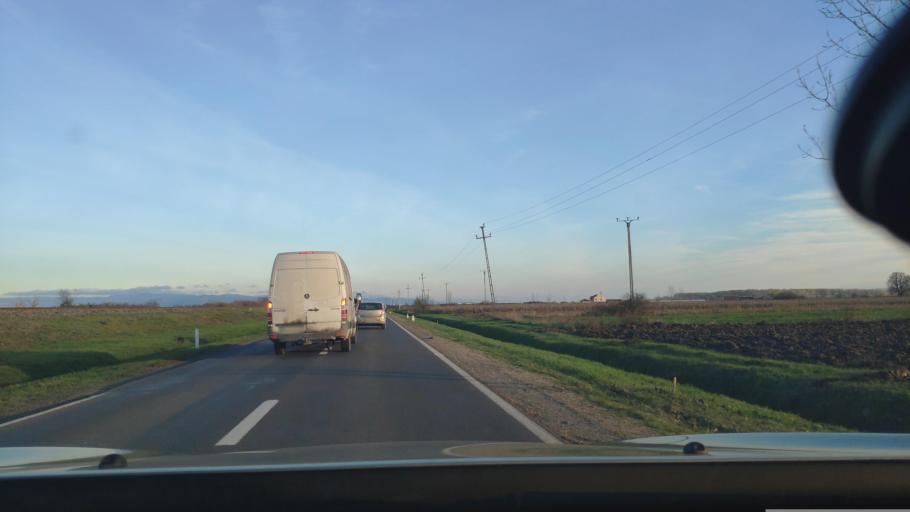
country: RO
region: Satu Mare
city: Culciu Mic
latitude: 47.7883
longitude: 23.0491
